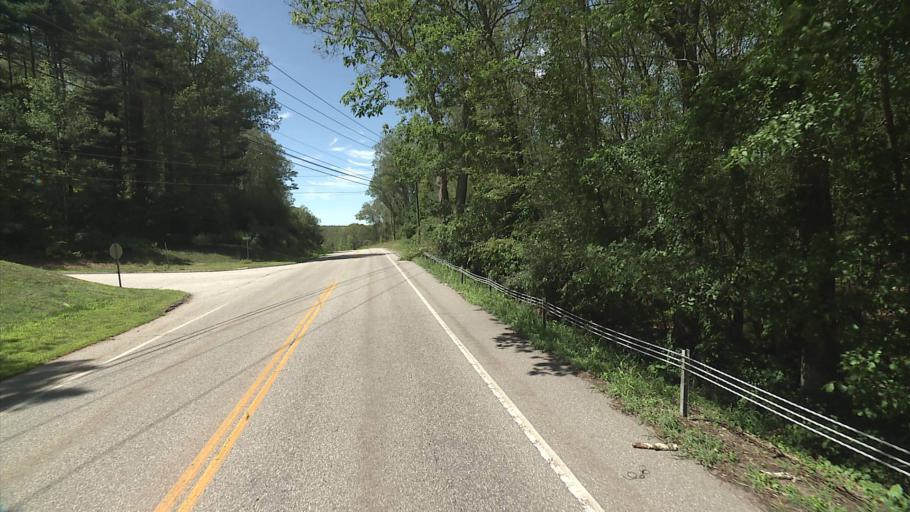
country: US
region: Connecticut
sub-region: Windham County
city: Putnam
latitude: 41.8528
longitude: -71.9464
